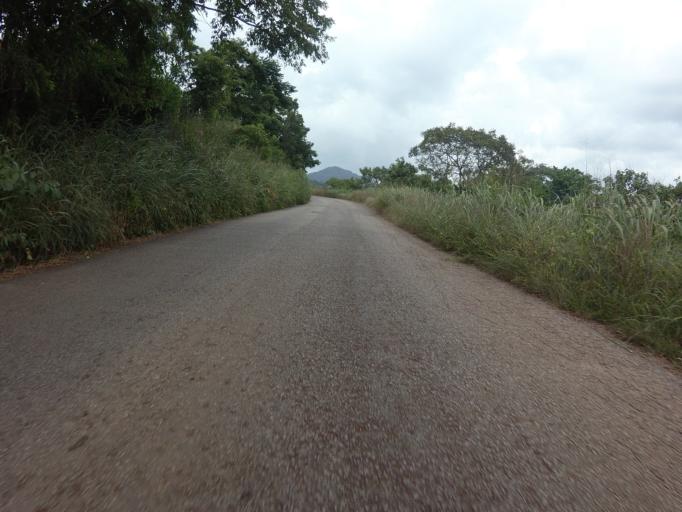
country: GH
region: Volta
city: Ho
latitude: 6.6793
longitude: 0.3531
